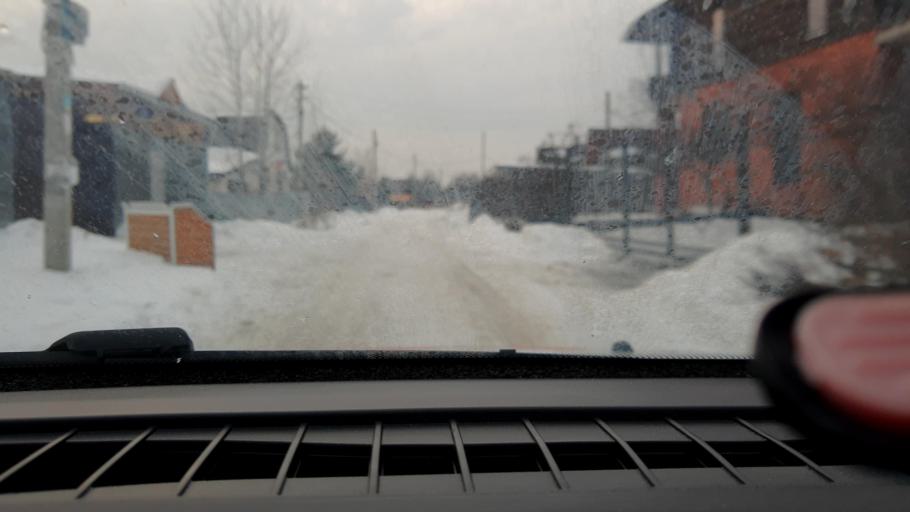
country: RU
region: Nizjnij Novgorod
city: Lukino
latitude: 56.4156
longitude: 43.6946
